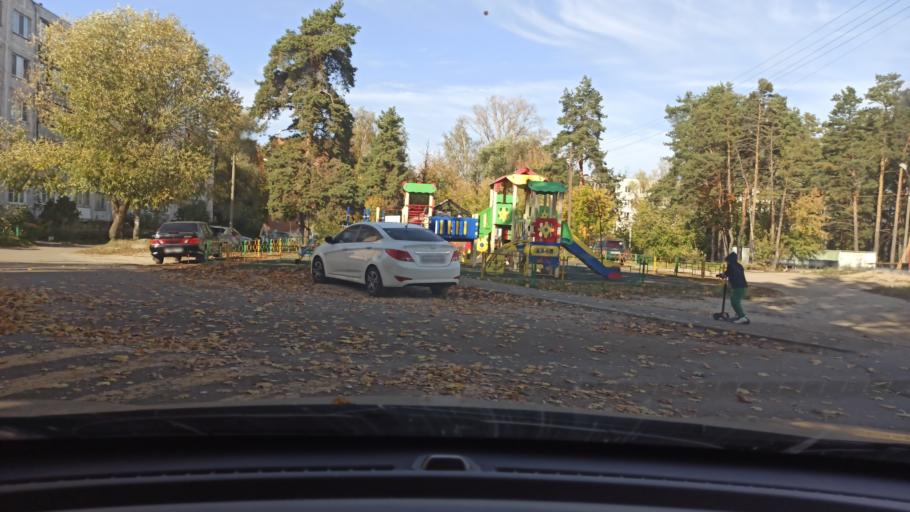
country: RU
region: Moskovskaya
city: Kurovskoye
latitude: 55.5822
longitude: 38.9356
